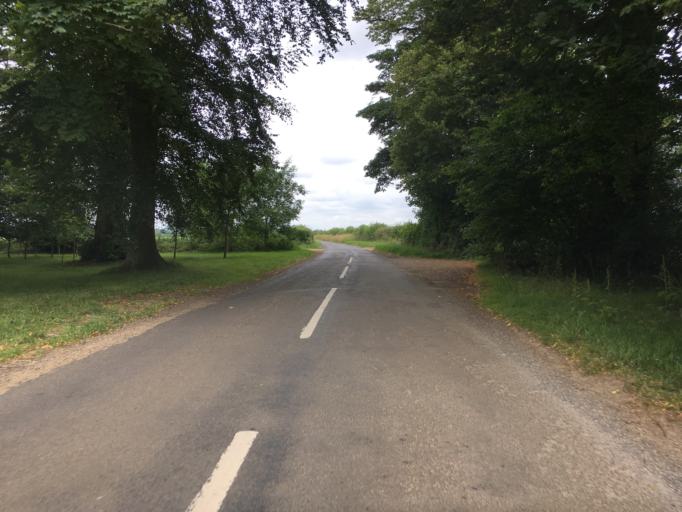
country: GB
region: England
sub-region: Oxfordshire
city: Hook Norton
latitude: 51.9556
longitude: -1.4316
